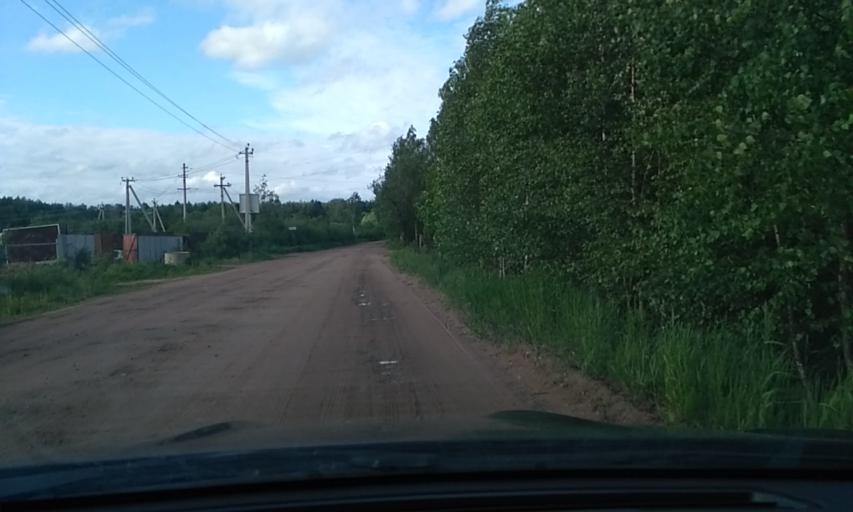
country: RU
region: Leningrad
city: Otradnoye
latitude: 59.8041
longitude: 30.8048
